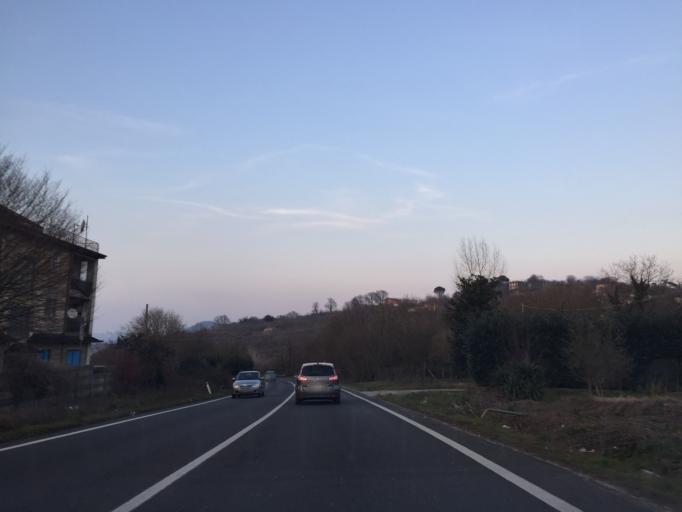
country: IT
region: Campania
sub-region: Provincia di Avellino
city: Avellino
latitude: 40.9035
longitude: 14.8072
